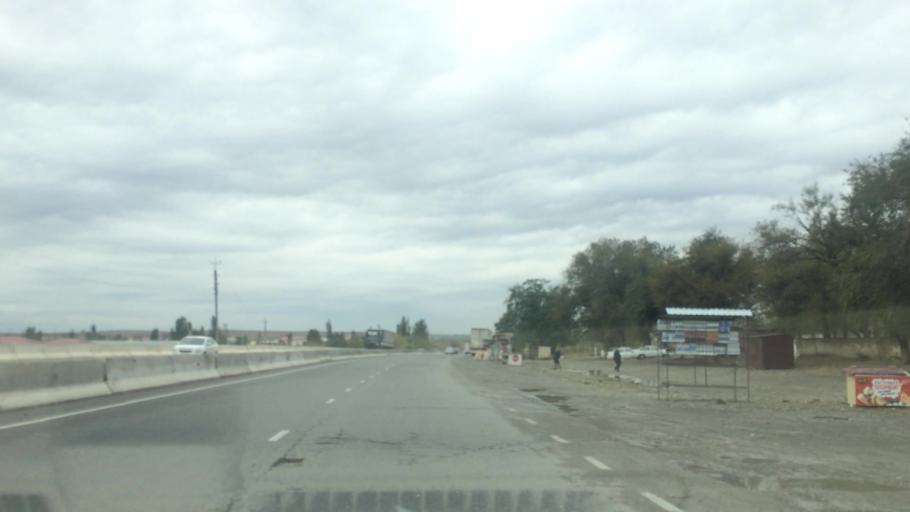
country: UZ
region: Jizzax
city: Jizzax
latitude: 39.9734
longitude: 67.5599
